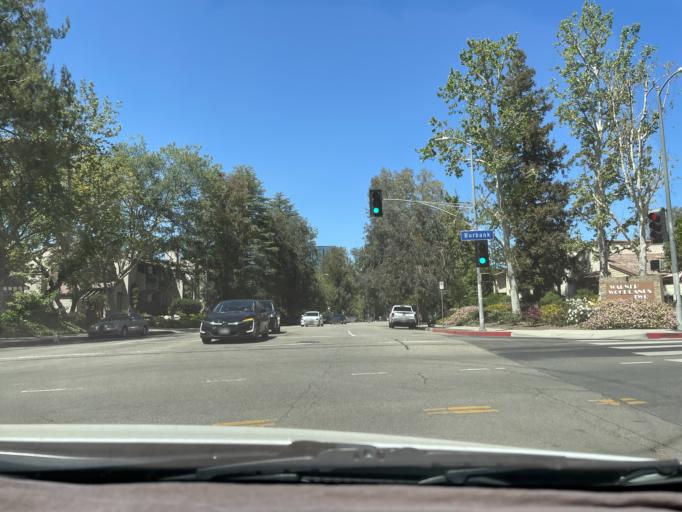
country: US
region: California
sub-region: Los Angeles County
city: Woodland Hills
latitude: 34.1732
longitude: -118.6019
